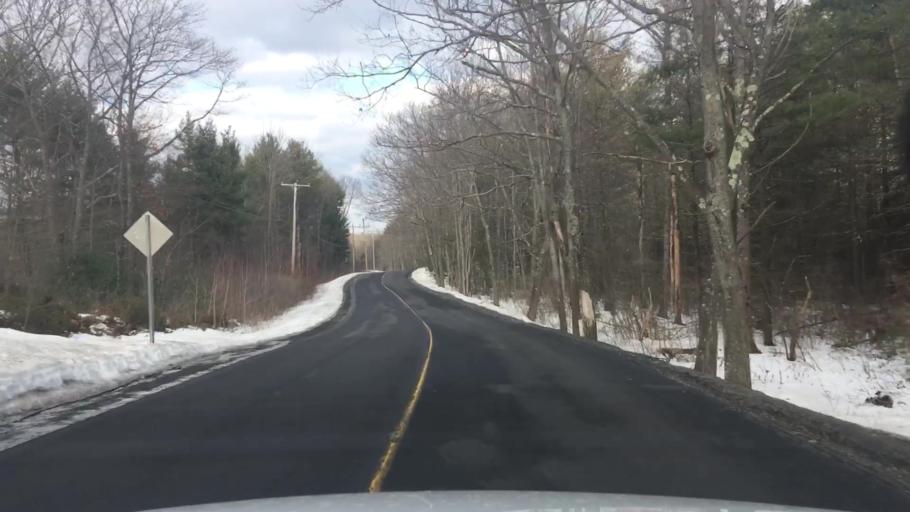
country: US
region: Maine
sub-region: York County
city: Arundel
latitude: 43.4198
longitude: -70.4623
